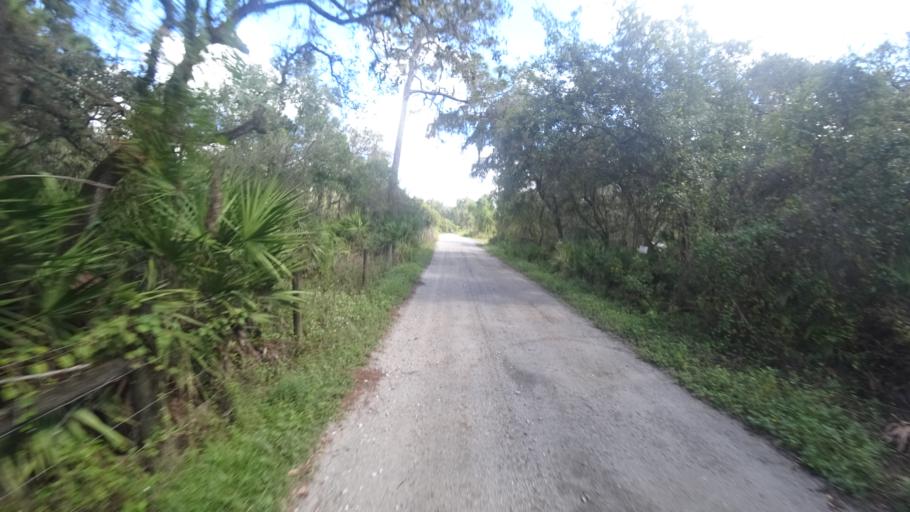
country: US
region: Florida
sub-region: Sarasota County
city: Lake Sarasota
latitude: 27.3285
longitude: -82.2646
